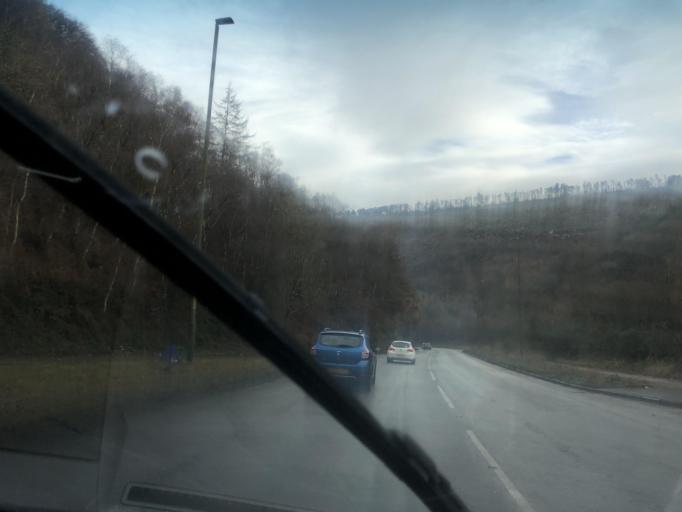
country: GB
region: Wales
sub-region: Caerphilly County Borough
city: Crumlin
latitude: 51.6833
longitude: -3.1067
